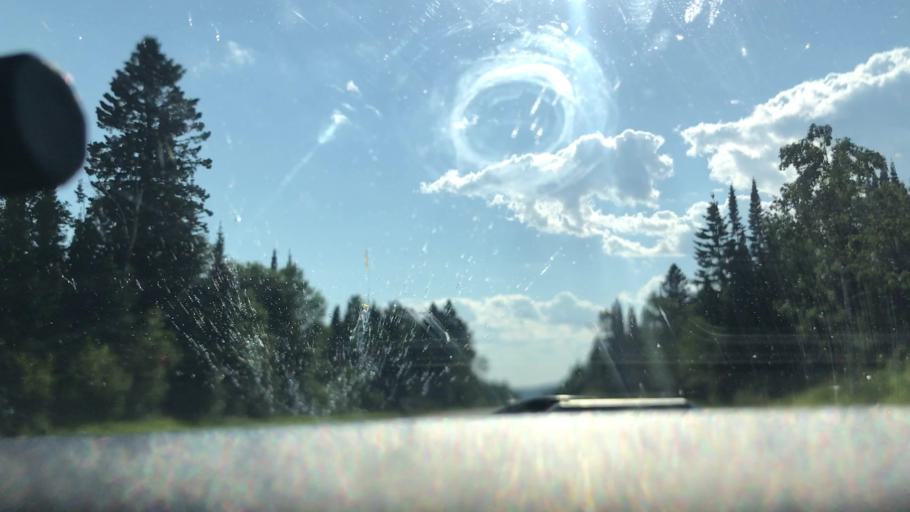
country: US
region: Minnesota
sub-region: Cook County
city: Grand Marais
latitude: 47.7965
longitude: -90.1243
